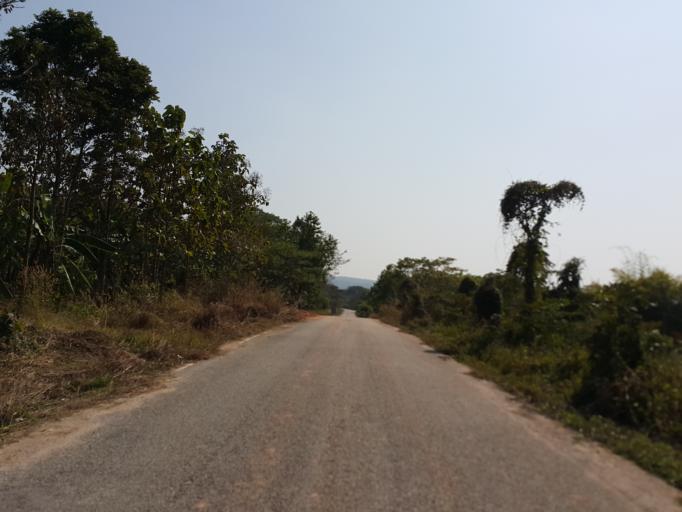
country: TH
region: Lampang
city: Wang Nuea
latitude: 19.0084
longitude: 99.6225
